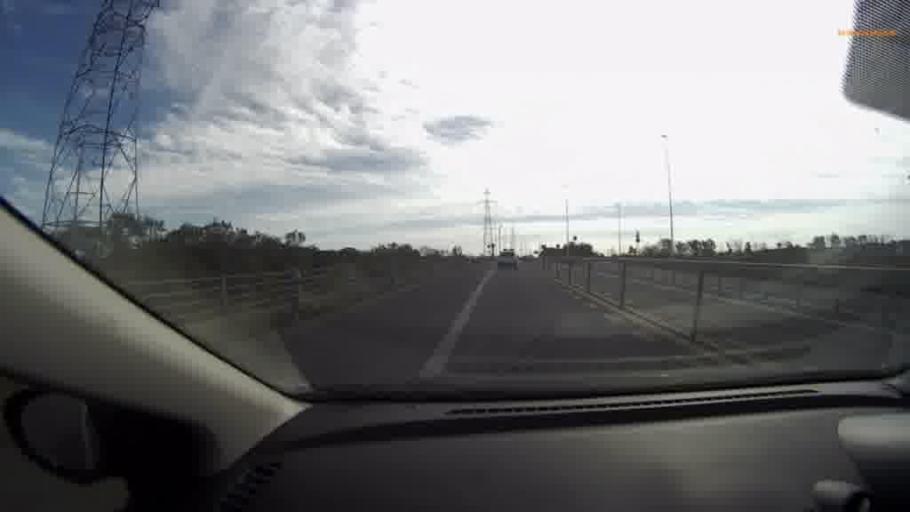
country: JP
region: Hokkaido
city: Kushiro
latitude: 43.0308
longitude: 144.4005
